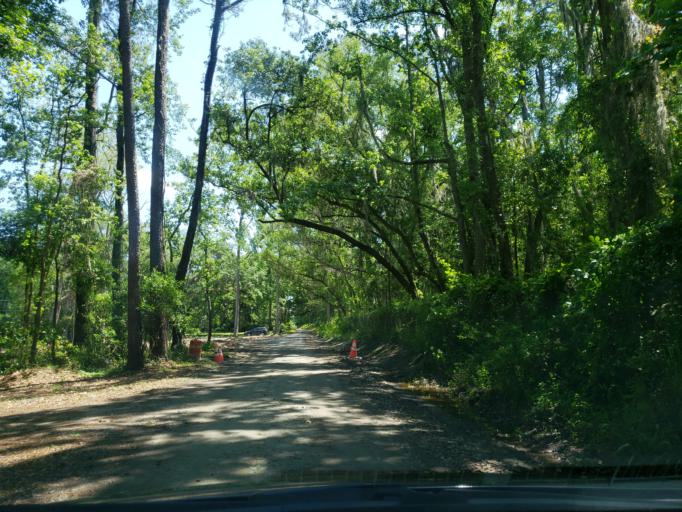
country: US
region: Georgia
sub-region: Chatham County
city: Whitemarsh Island
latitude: 32.0536
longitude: -81.0196
